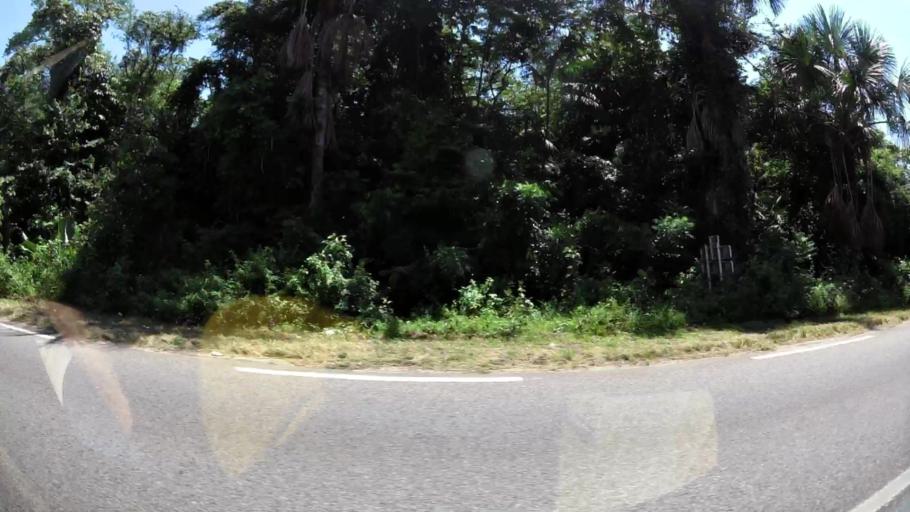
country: GF
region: Guyane
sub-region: Guyane
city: Cayenne
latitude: 4.9100
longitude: -52.3243
